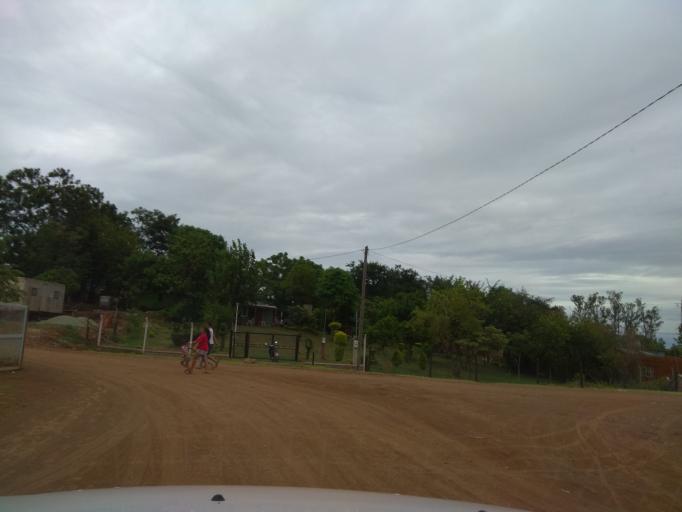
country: AR
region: Misiones
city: Garupa
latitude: -27.4369
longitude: -55.8631
